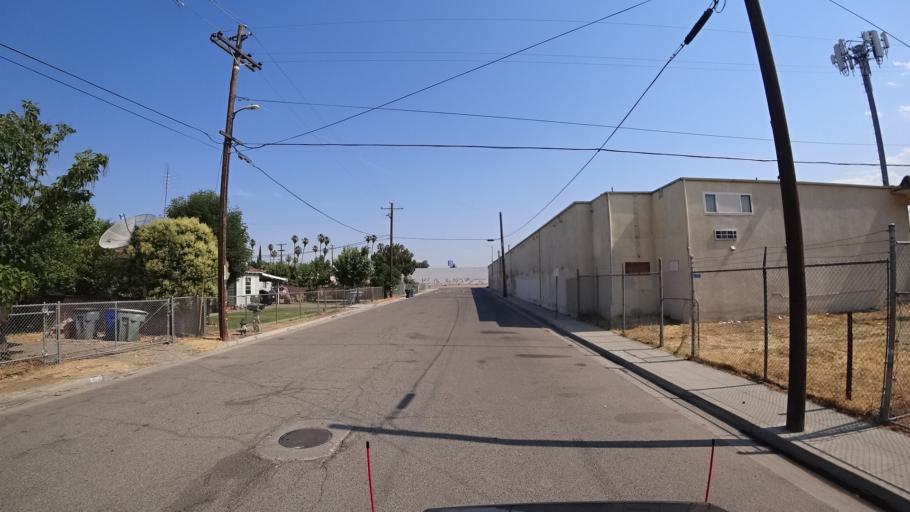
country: US
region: California
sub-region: Fresno County
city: West Park
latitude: 36.7543
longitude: -119.8297
